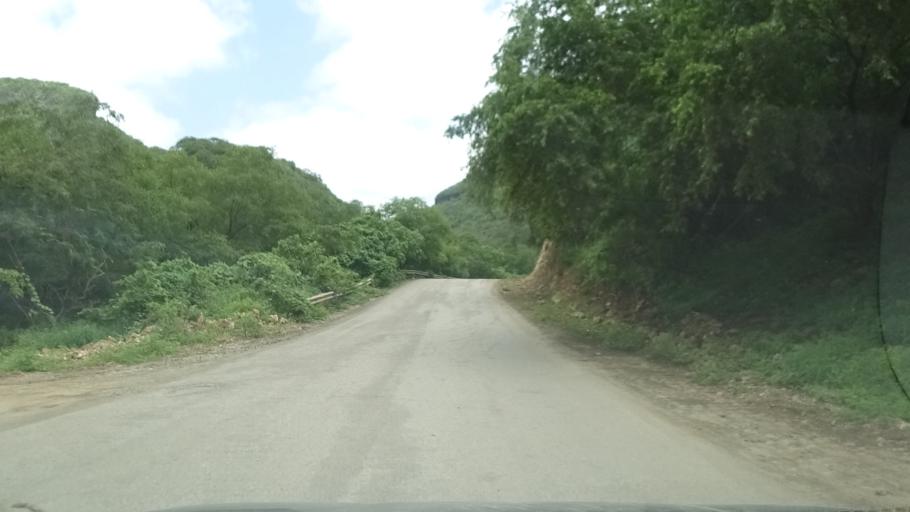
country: OM
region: Zufar
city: Salalah
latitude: 17.1604
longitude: 54.1690
